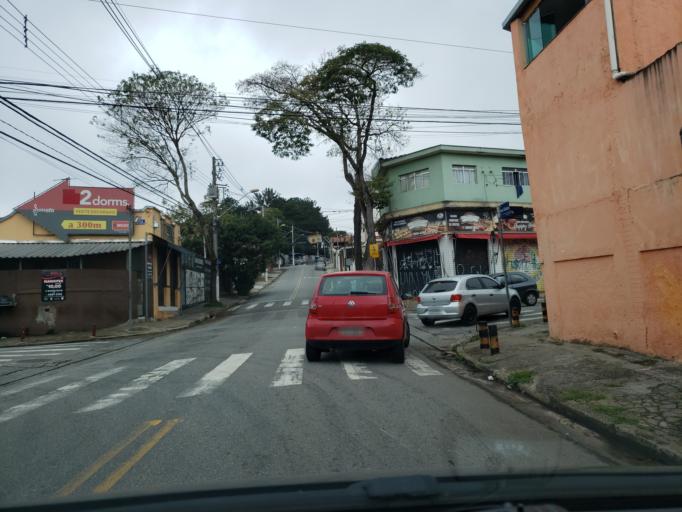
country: BR
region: Sao Paulo
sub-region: Santo Andre
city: Santo Andre
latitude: -23.6416
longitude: -46.5299
